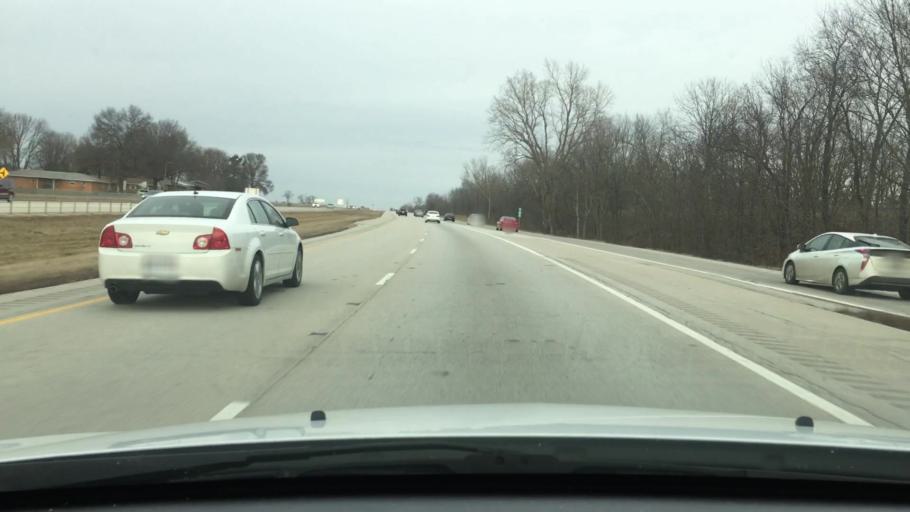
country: US
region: Illinois
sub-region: Sangamon County
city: Sherman
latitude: 39.9174
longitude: -89.5823
